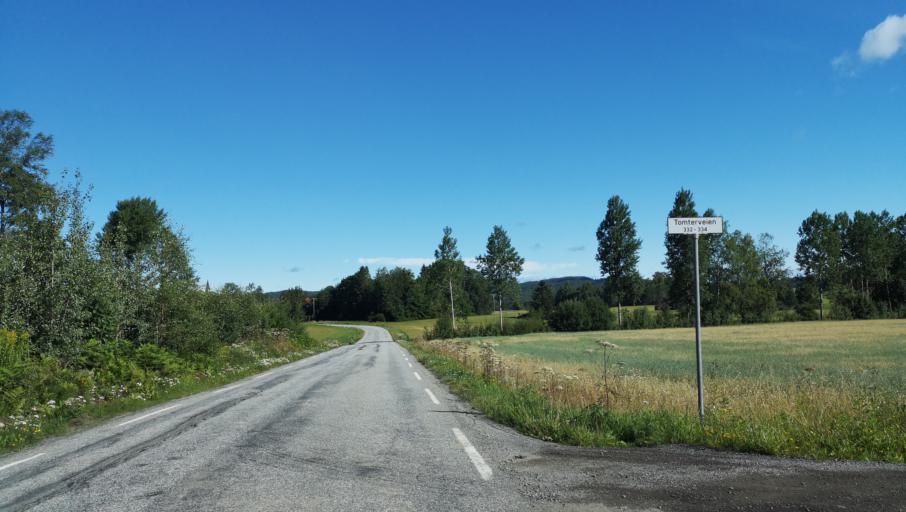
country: NO
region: Ostfold
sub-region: Hobol
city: Tomter
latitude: 59.6470
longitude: 11.0144
